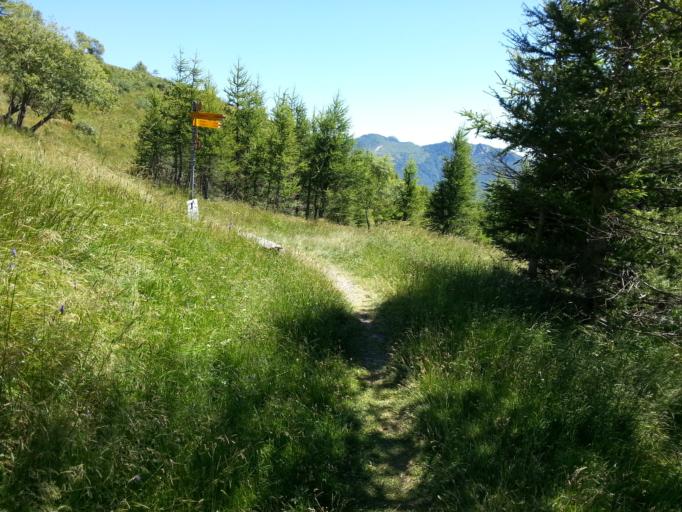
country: CH
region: Ticino
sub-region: Bellinzona District
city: Camorino
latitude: 46.1089
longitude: 9.0337
